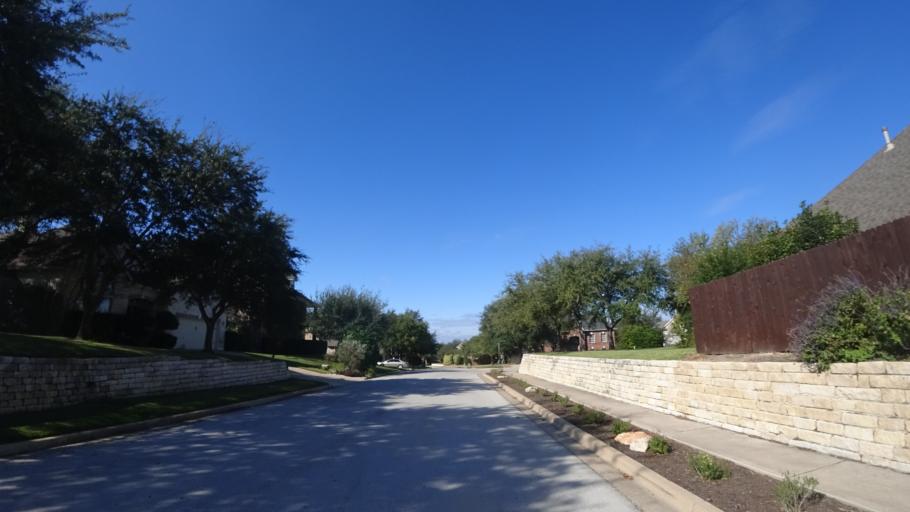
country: US
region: Texas
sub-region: Travis County
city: Hudson Bend
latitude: 30.3756
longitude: -97.8956
